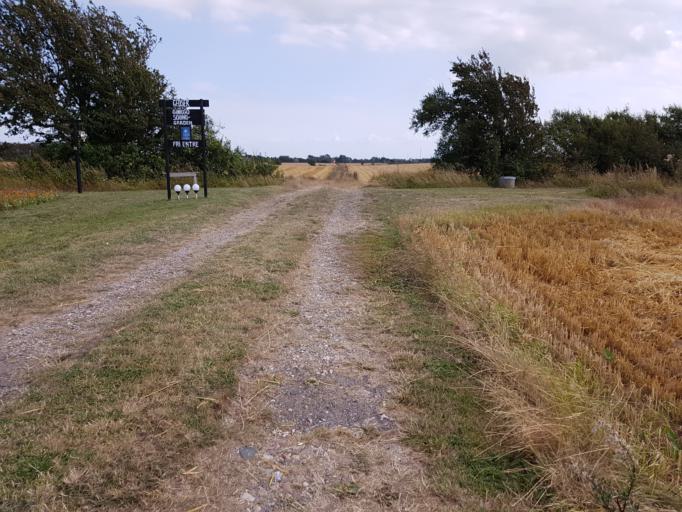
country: DK
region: Zealand
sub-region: Guldborgsund Kommune
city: Nykobing Falster
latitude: 54.5979
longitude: 11.9231
